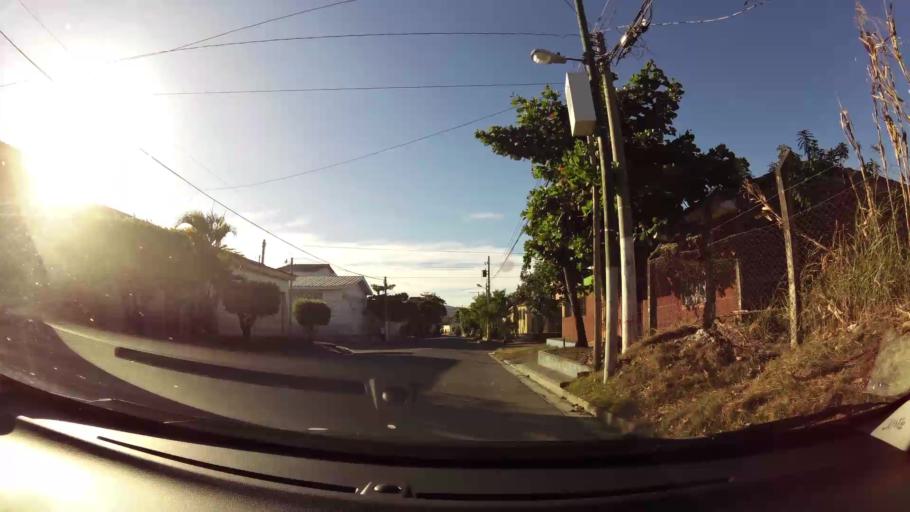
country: SV
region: Santa Ana
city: Metapan
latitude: 14.3265
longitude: -89.4437
